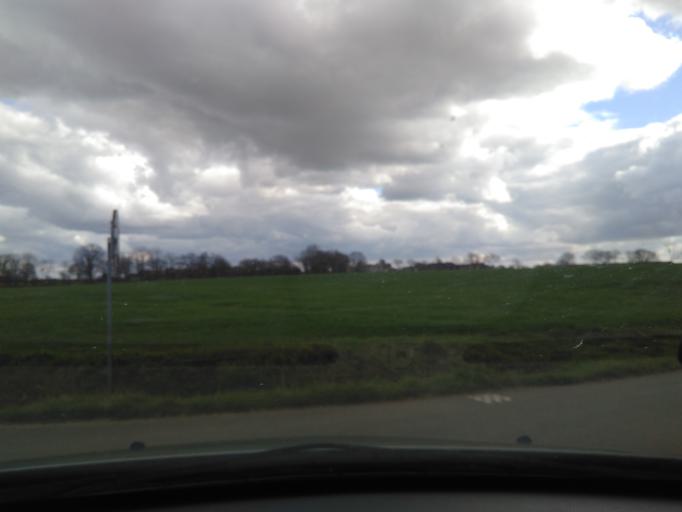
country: FR
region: Pays de la Loire
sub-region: Departement de la Vendee
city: Chantonnay
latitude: 46.6912
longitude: -1.0989
